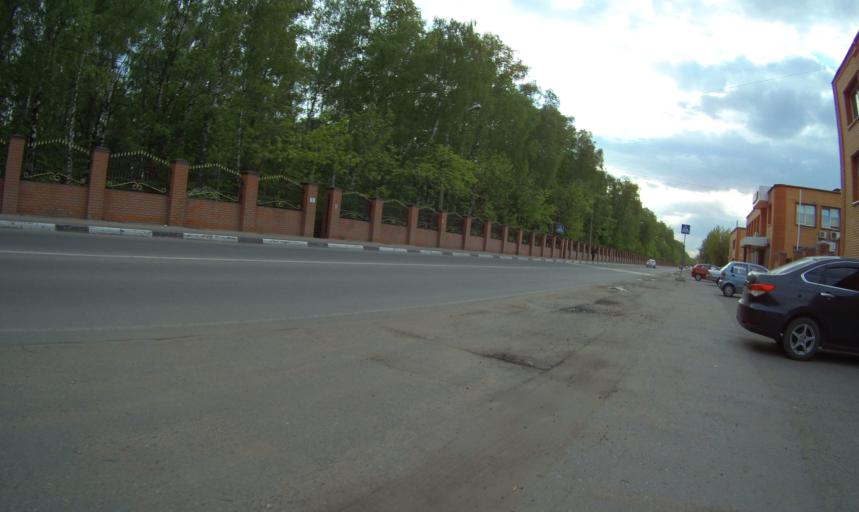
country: RU
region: Moskovskaya
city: Ramenskoye
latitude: 55.5686
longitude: 38.2594
